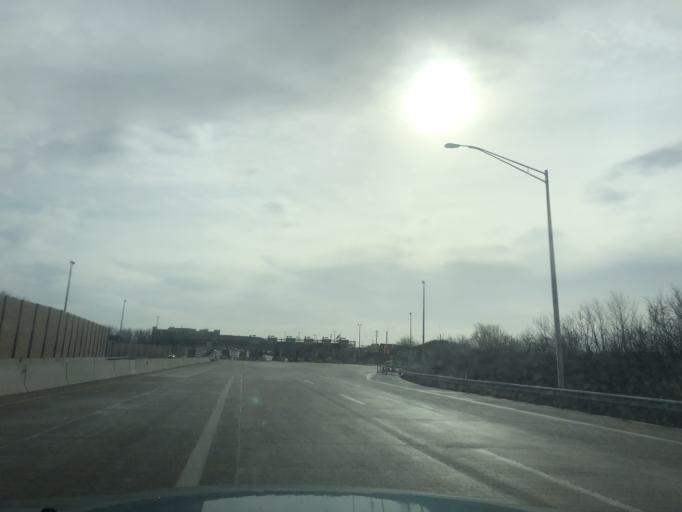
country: US
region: Pennsylvania
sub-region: Montgomery County
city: Kulpsville
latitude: 40.2512
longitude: -75.3451
